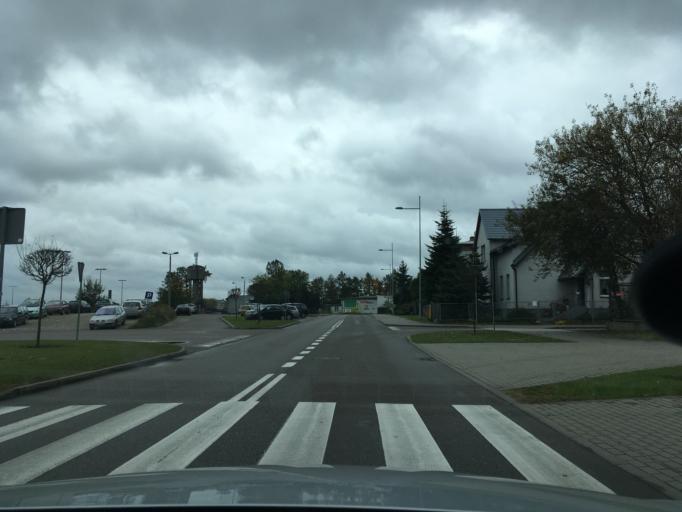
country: PL
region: Pomeranian Voivodeship
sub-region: Powiat koscierski
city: Koscierzyna
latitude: 54.1208
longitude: 17.9933
